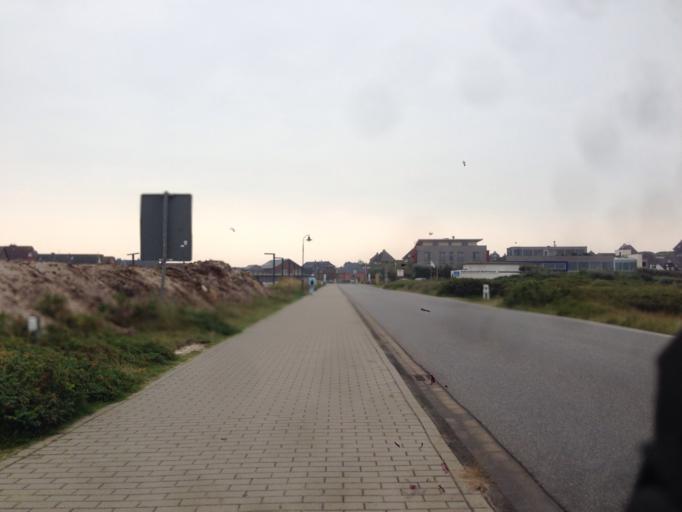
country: DE
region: Schleswig-Holstein
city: Norddorf
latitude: 54.7599
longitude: 8.2860
